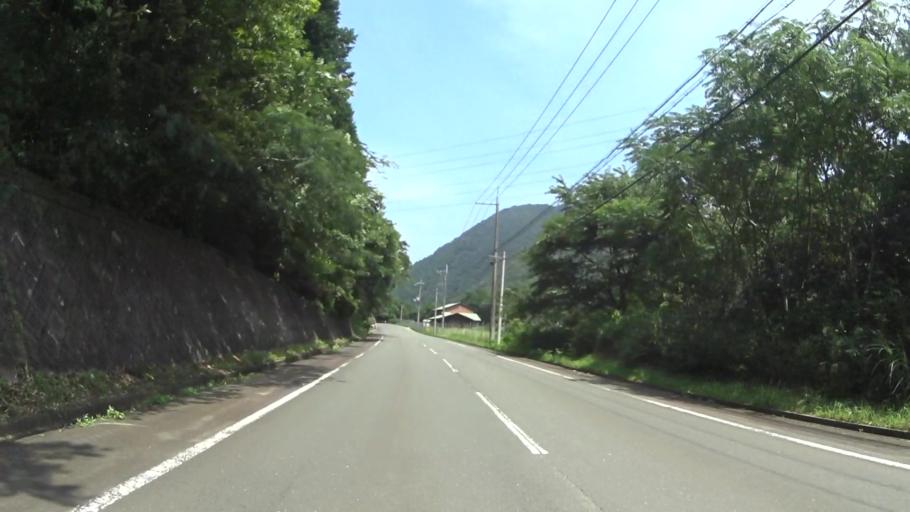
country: JP
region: Kyoto
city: Ayabe
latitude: 35.2764
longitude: 135.4316
